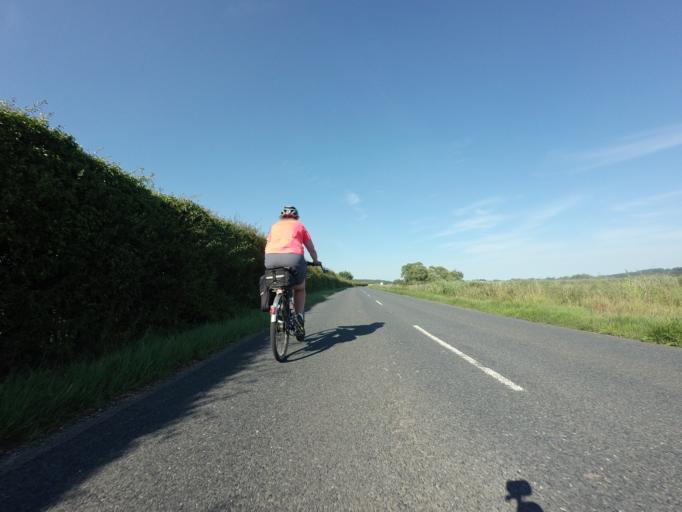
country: GB
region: England
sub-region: Kent
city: Tenterden
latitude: 51.0340
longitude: 0.6908
